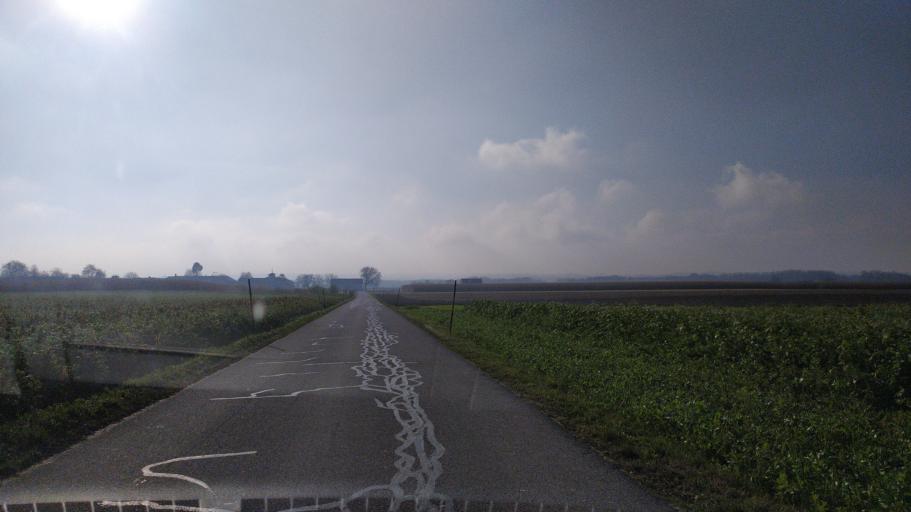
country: AT
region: Upper Austria
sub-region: Politischer Bezirk Perg
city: Perg
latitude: 48.2001
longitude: 14.6517
